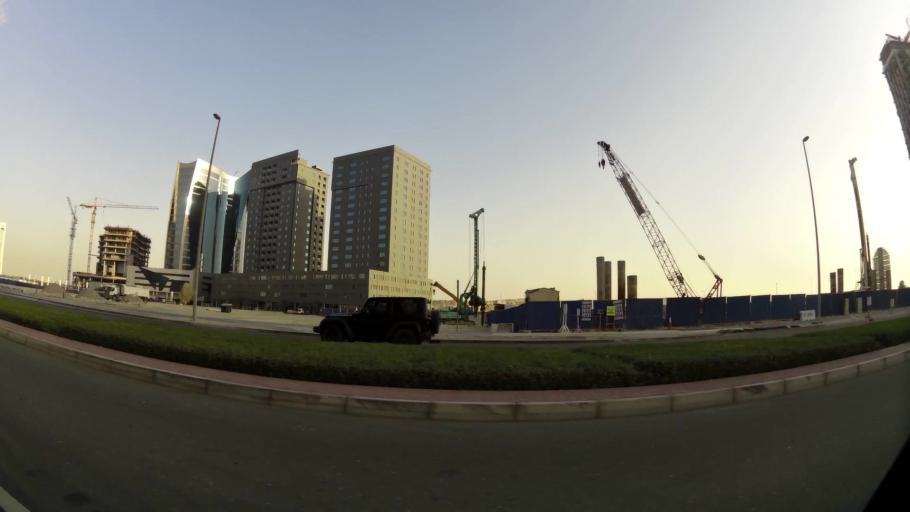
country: AE
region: Dubai
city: Dubai
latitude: 25.1802
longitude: 55.2661
